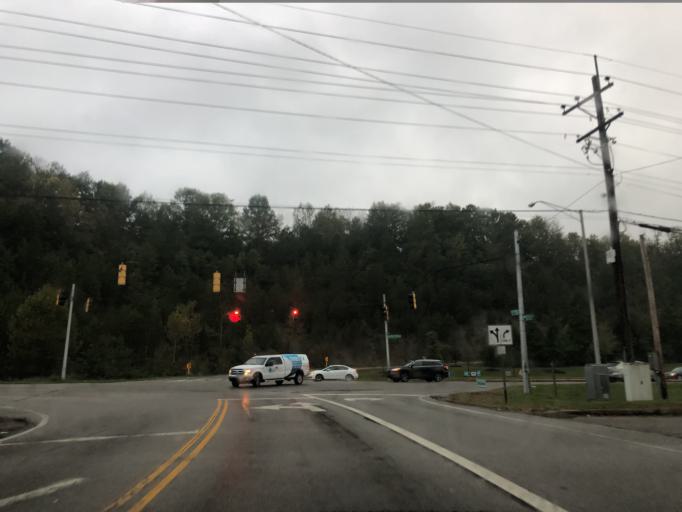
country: US
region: Ohio
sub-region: Hamilton County
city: The Village of Indian Hill
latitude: 39.2472
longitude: -84.2966
